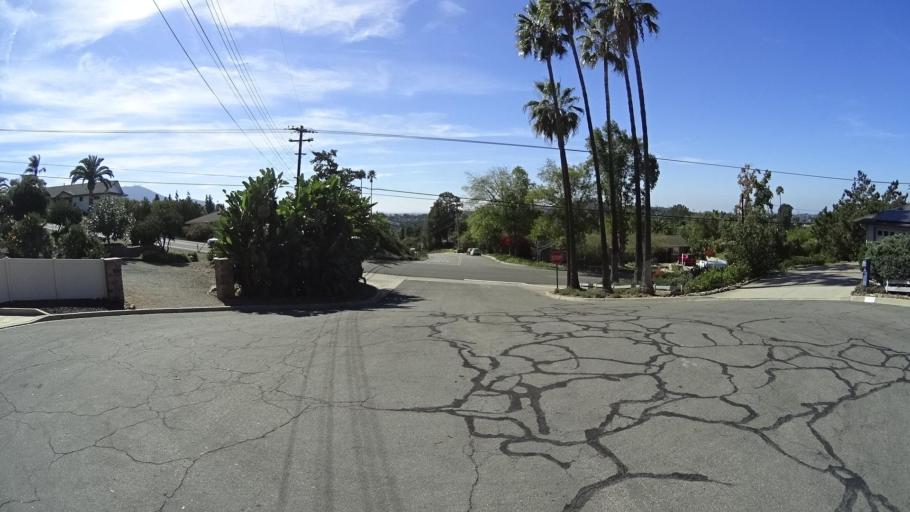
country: US
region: California
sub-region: San Diego County
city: Casa de Oro-Mount Helix
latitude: 32.7573
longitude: -116.9547
